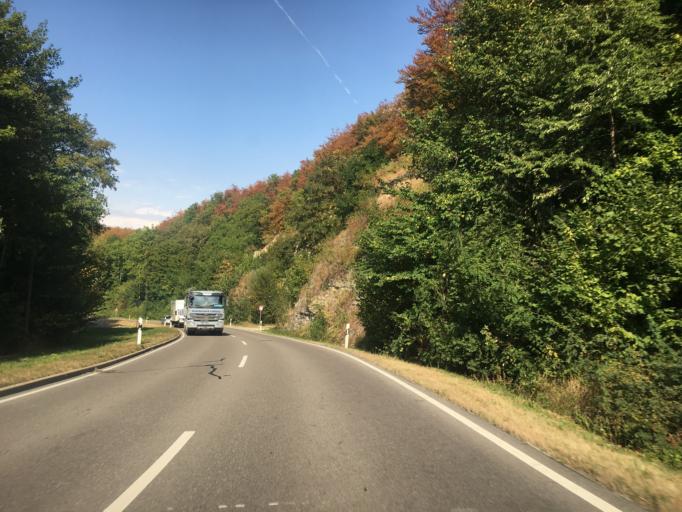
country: DE
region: Baden-Wuerttemberg
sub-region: Tuebingen Region
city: Pfullingen
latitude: 48.4162
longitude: 9.1816
